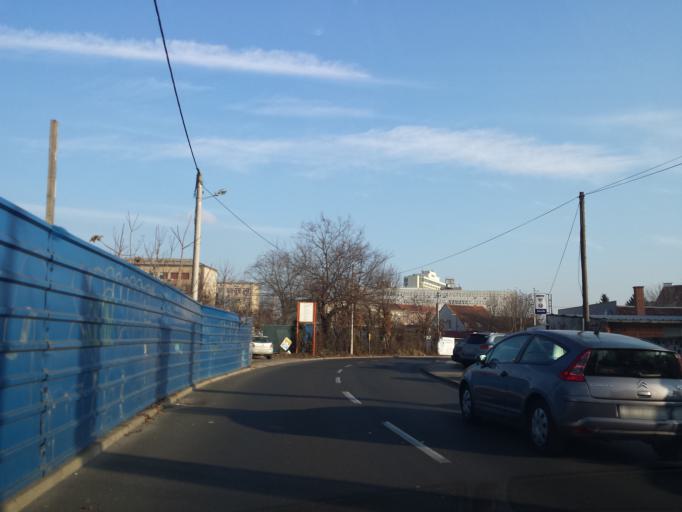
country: HR
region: Grad Zagreb
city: Zagreb - Centar
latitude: 45.8075
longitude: 15.9595
